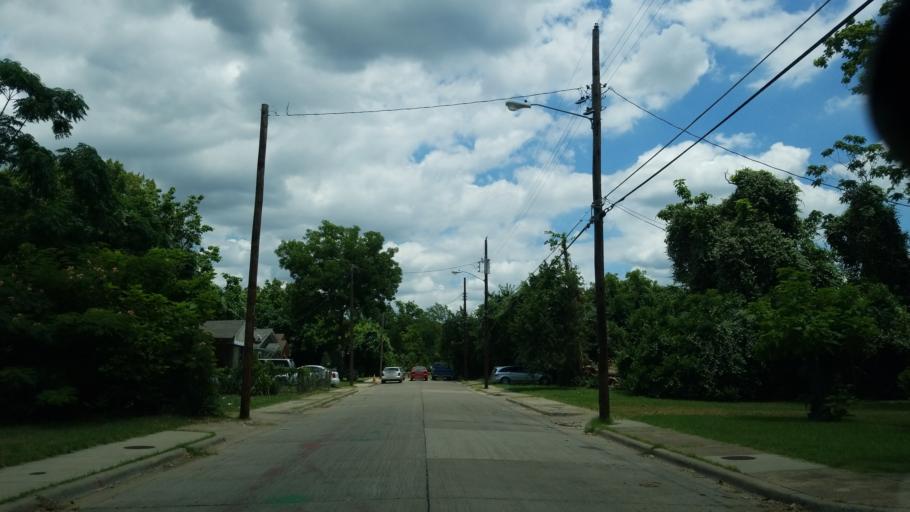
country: US
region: Texas
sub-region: Dallas County
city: Dallas
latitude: 32.7487
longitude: -96.7503
